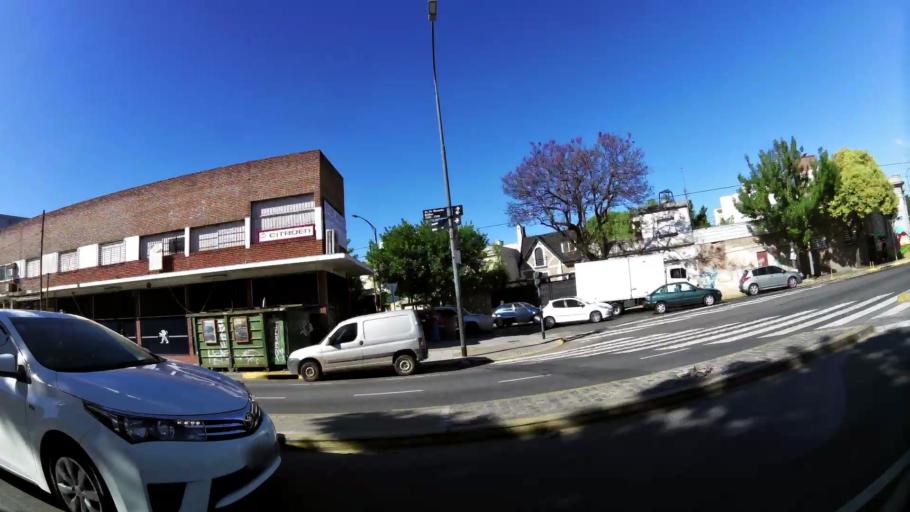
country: AR
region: Buenos Aires F.D.
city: Colegiales
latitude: -34.5590
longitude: -58.4740
